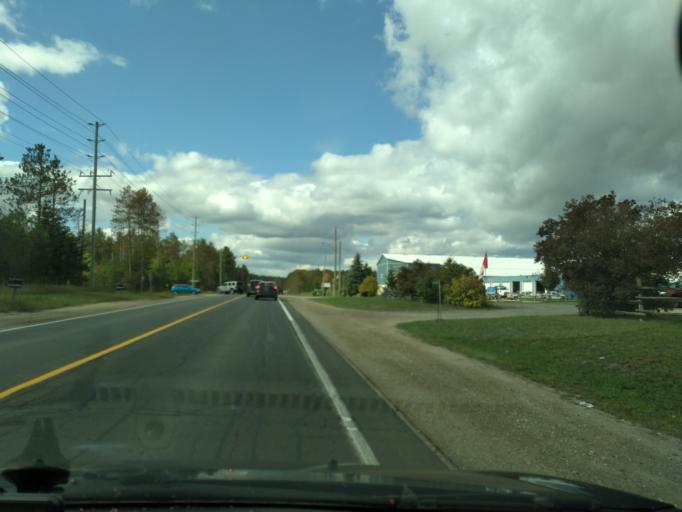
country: CA
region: Ontario
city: Angus
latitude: 44.2539
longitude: -79.7985
